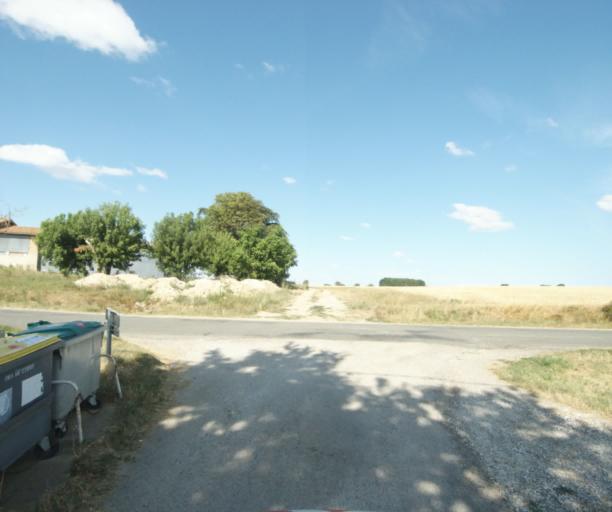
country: FR
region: Midi-Pyrenees
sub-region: Departement du Tarn
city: Puylaurens
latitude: 43.5314
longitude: 1.9732
